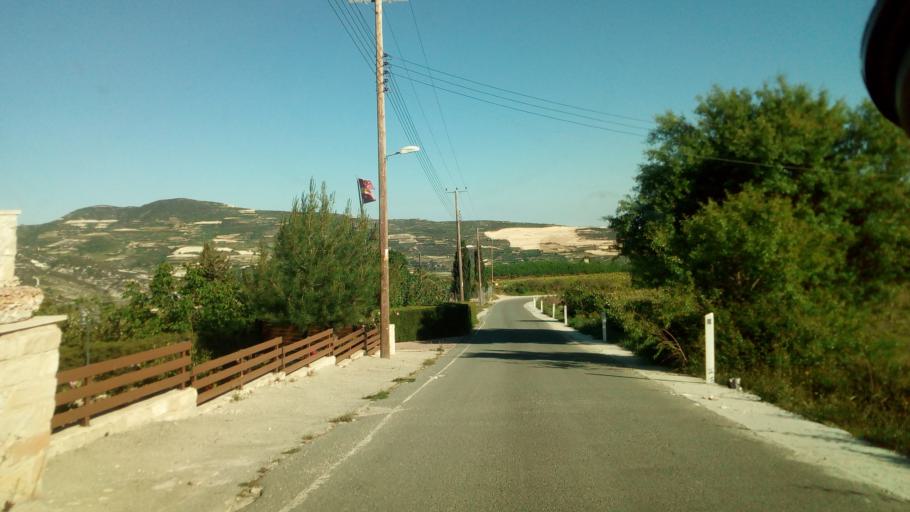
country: CY
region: Limassol
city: Pachna
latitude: 34.8608
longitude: 32.8033
